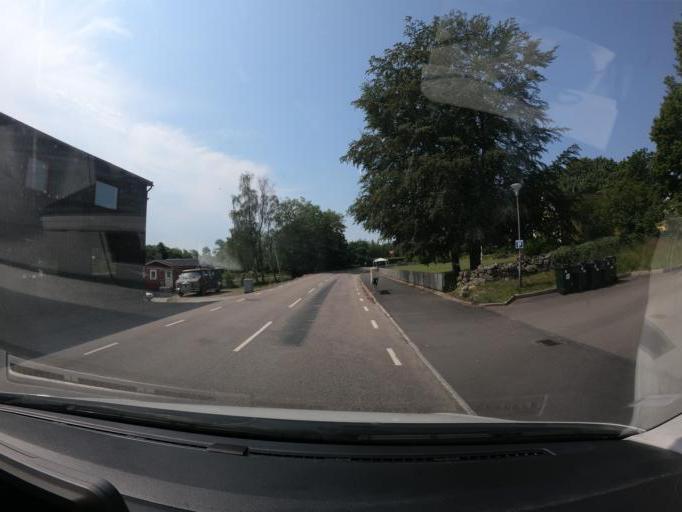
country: SE
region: Skane
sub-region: Hassleholms Kommun
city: Tormestorp
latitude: 56.1582
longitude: 13.6816
